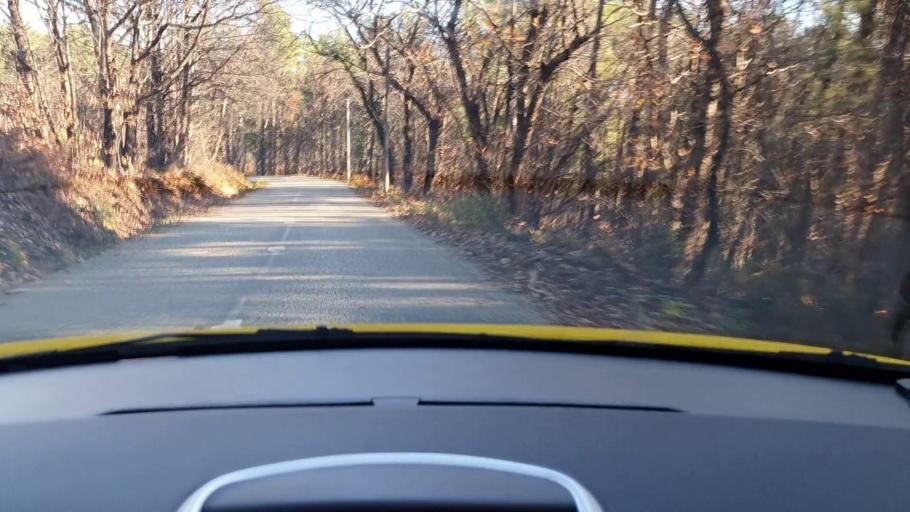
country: FR
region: Languedoc-Roussillon
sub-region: Departement du Gard
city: Branoux-les-Taillades
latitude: 44.2828
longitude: 3.9618
